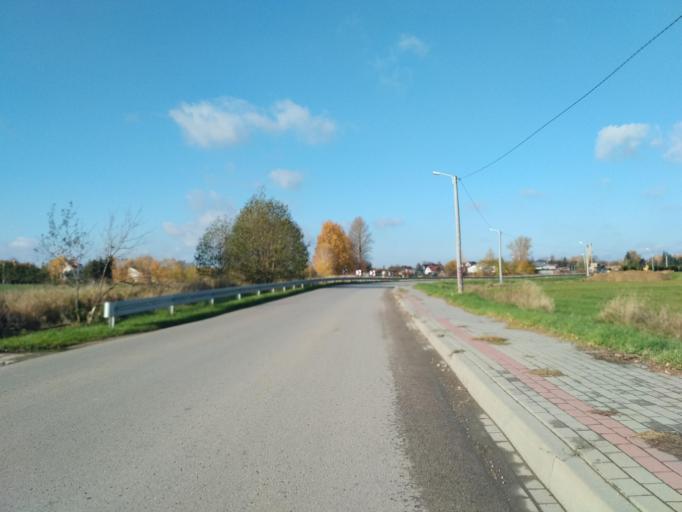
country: PL
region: Subcarpathian Voivodeship
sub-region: Powiat rzeszowski
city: Niechobrz
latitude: 50.0167
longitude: 21.8864
